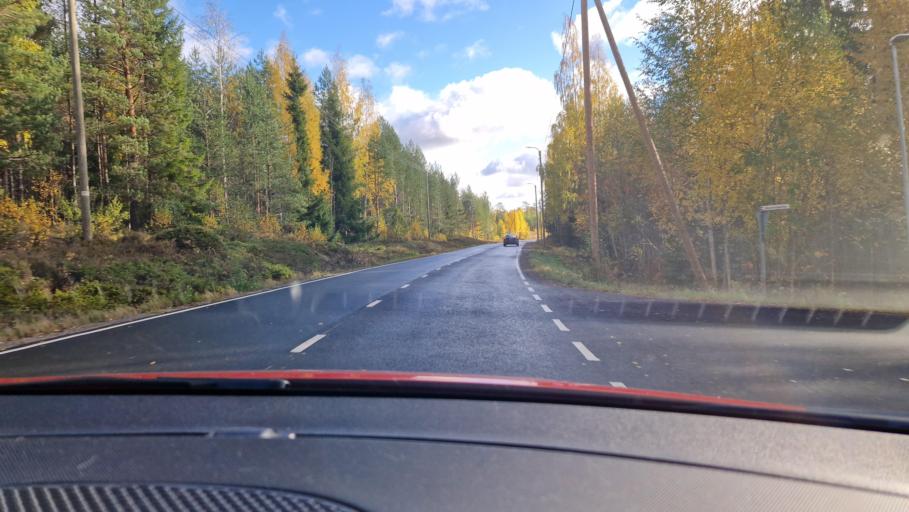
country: FI
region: South Karelia
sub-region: Lappeenranta
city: Lemi
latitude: 60.9652
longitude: 27.7694
